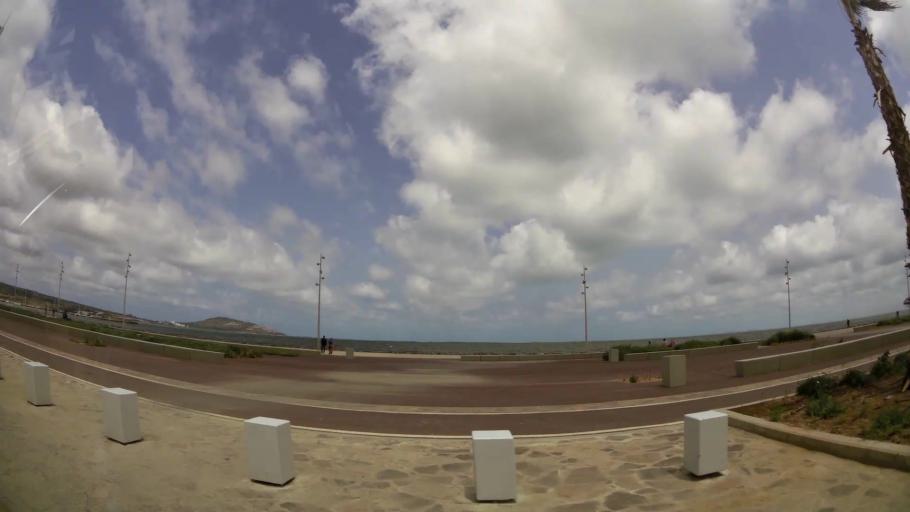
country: MA
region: Oriental
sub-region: Nador
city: Nador
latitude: 35.1829
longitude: -2.9240
